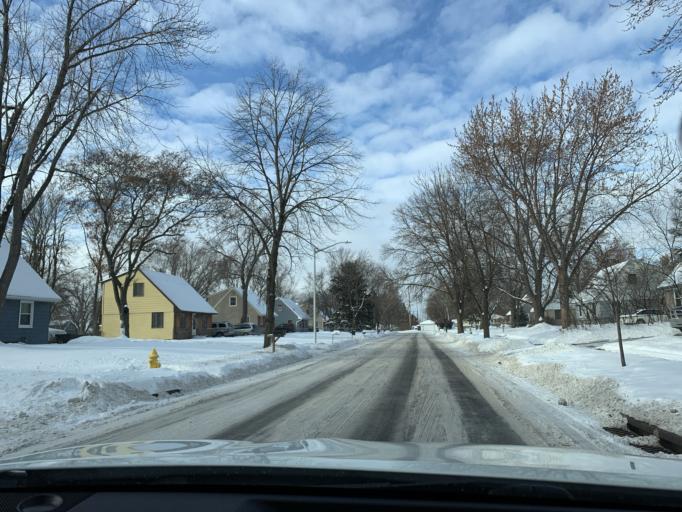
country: US
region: Minnesota
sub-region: Anoka County
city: Coon Rapids
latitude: 45.1679
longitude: -93.2839
